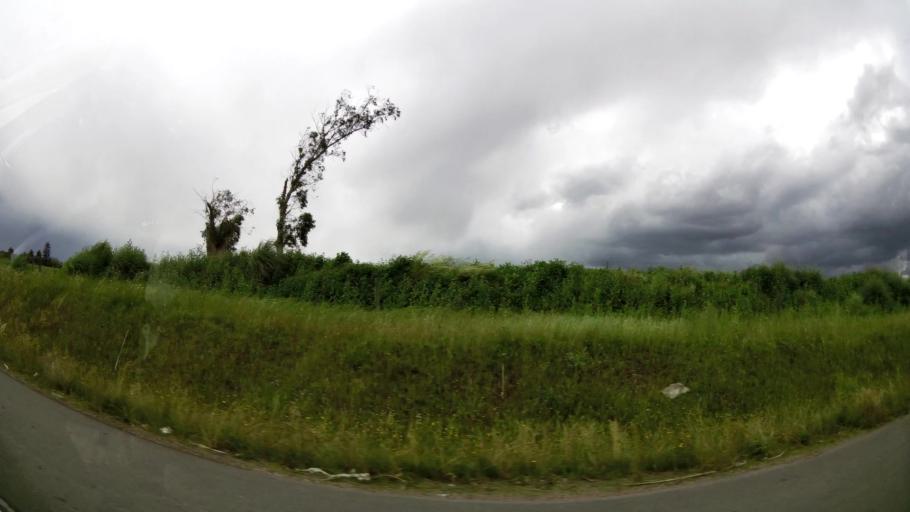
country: UY
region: Canelones
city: Toledo
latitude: -34.7951
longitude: -56.1302
